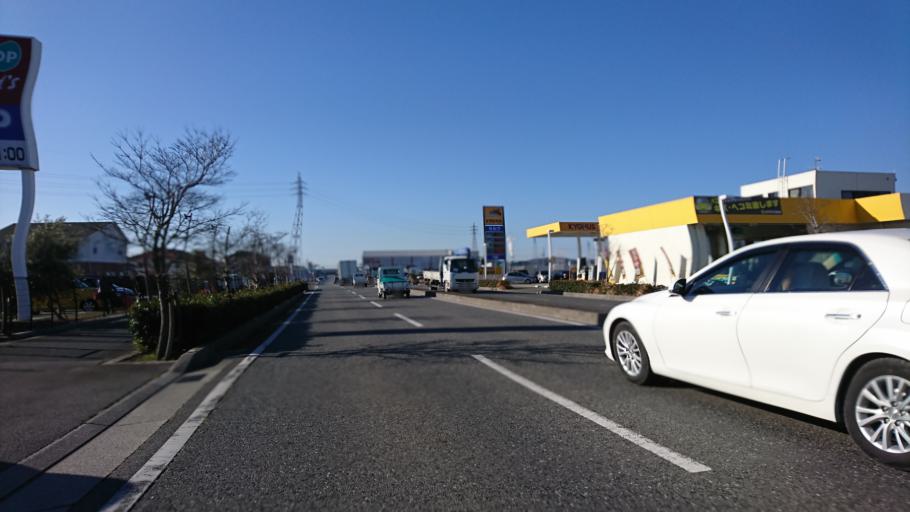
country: JP
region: Hyogo
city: Kakogawacho-honmachi
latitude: 34.7919
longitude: 134.8235
